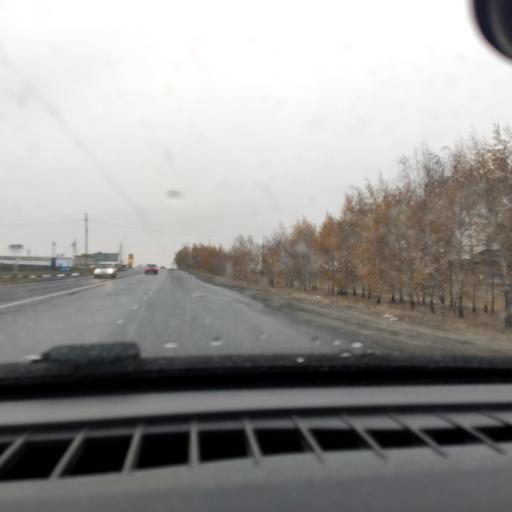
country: RU
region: Belgorod
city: Alekseyevka
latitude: 50.6445
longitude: 38.6839
